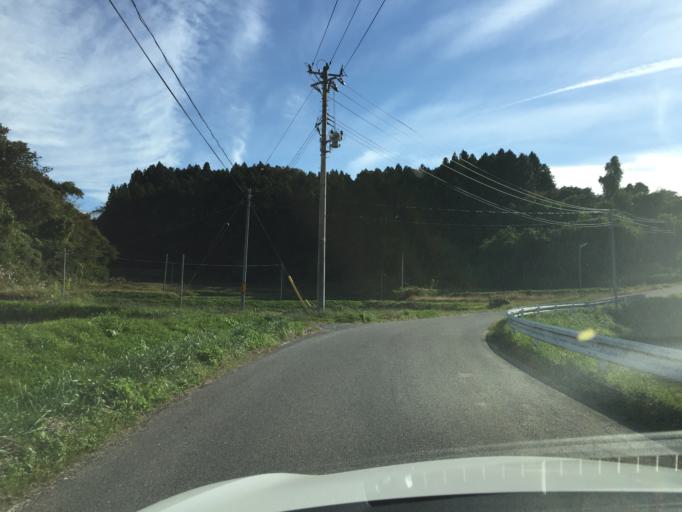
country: JP
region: Fukushima
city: Miharu
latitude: 37.3441
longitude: 140.4964
